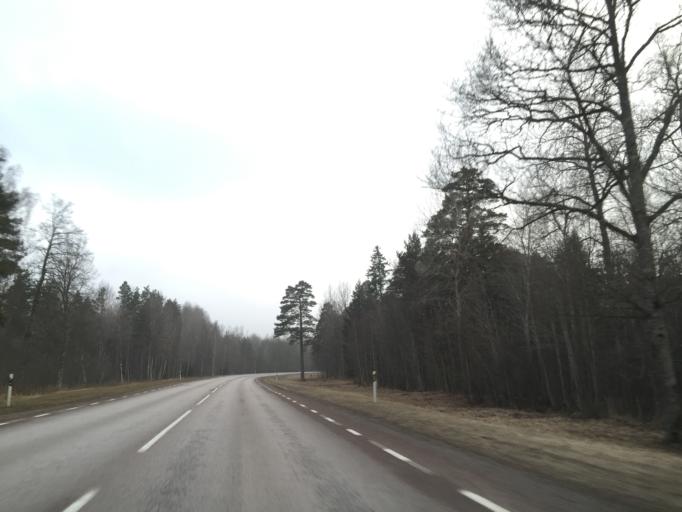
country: EE
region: Saare
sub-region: Kuressaare linn
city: Kuressaare
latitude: 58.3360
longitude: 22.6671
